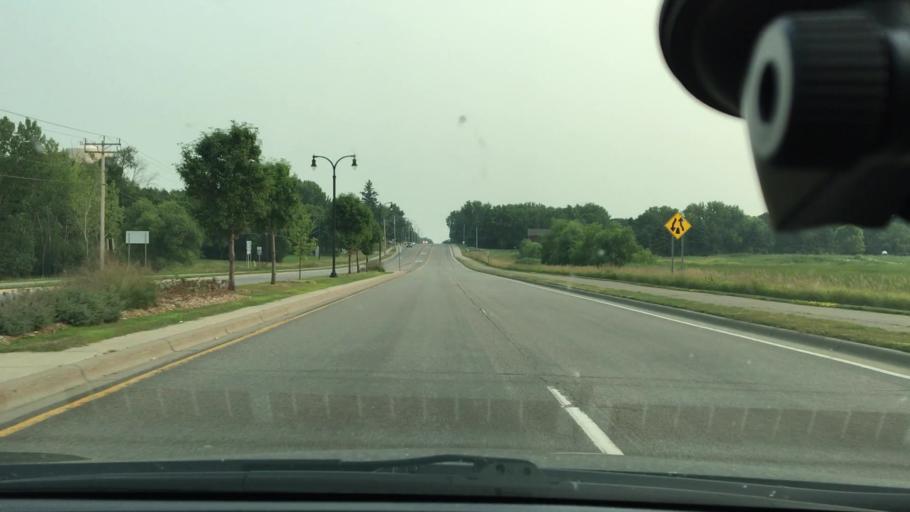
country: US
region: Minnesota
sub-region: Wright County
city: Saint Michael
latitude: 45.2233
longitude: -93.6646
